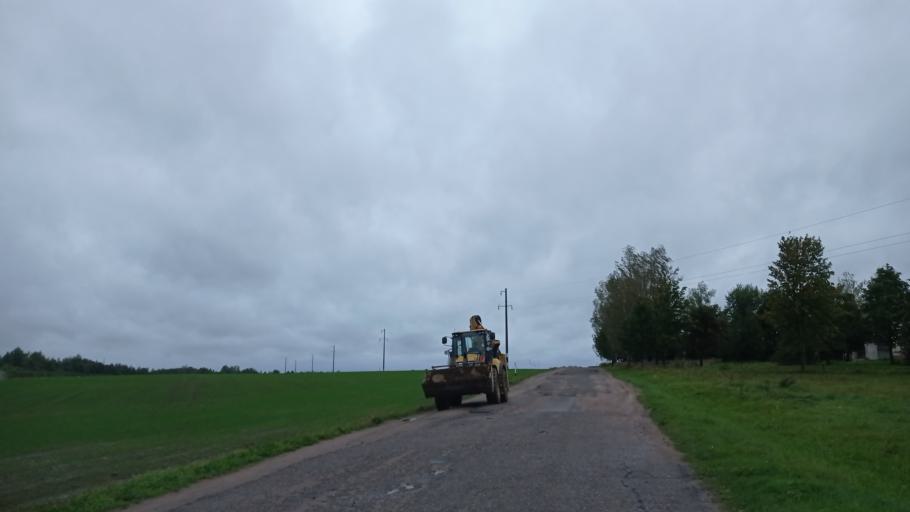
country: BY
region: Vitebsk
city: Haradok
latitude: 55.3370
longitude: 30.0940
